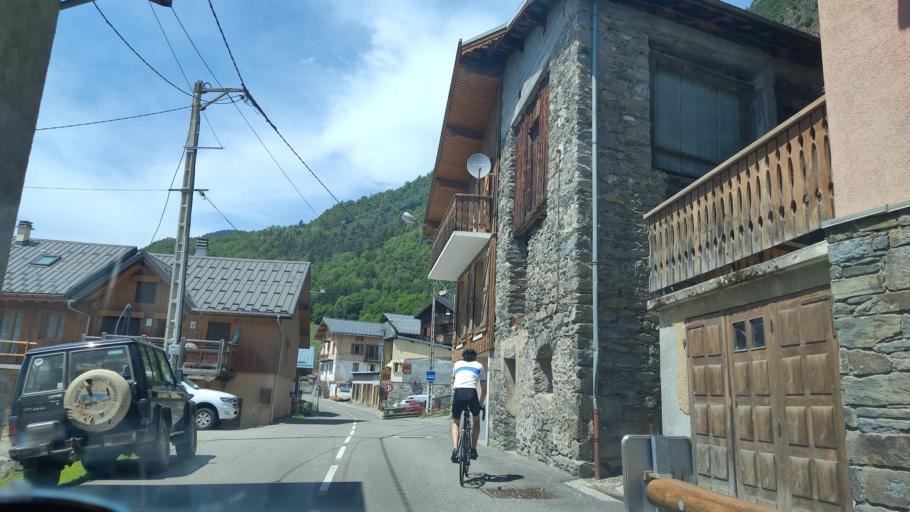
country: FR
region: Rhone-Alpes
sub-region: Departement de la Savoie
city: Les Allues
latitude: 45.4560
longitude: 6.5903
